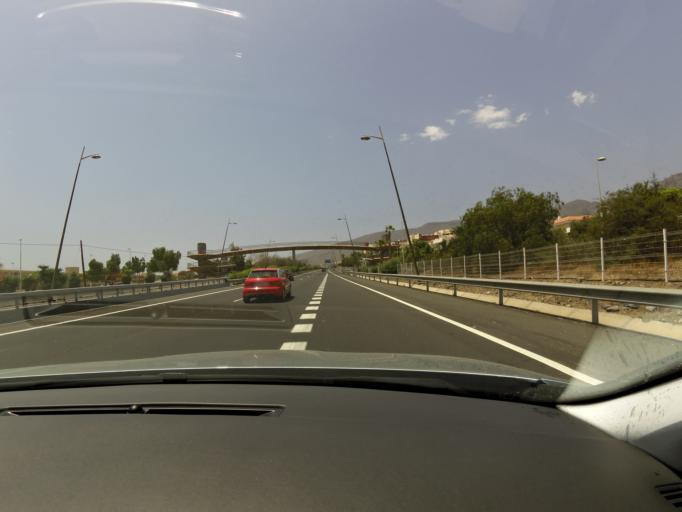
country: ES
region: Canary Islands
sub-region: Provincia de Santa Cruz de Tenerife
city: Playa de las Americas
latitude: 28.0918
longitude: -16.7294
